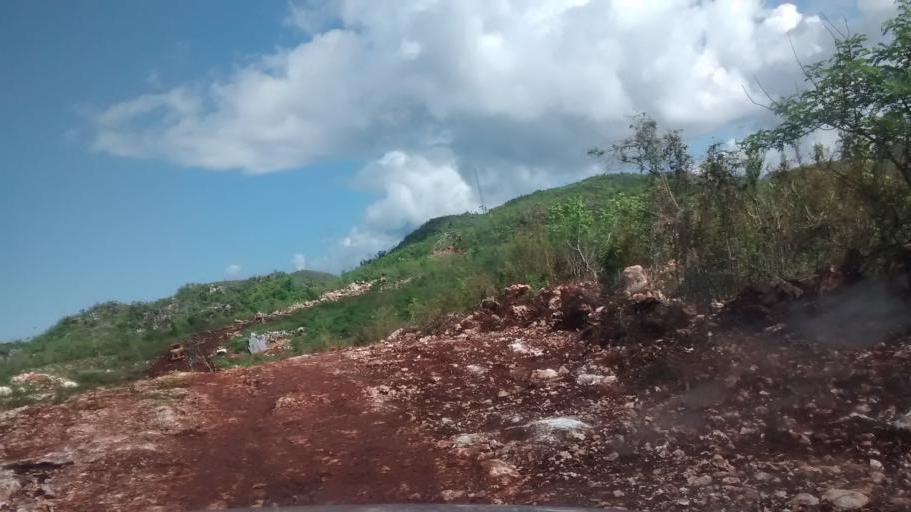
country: HT
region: Grandans
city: Corail
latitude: 18.5400
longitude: -73.9240
